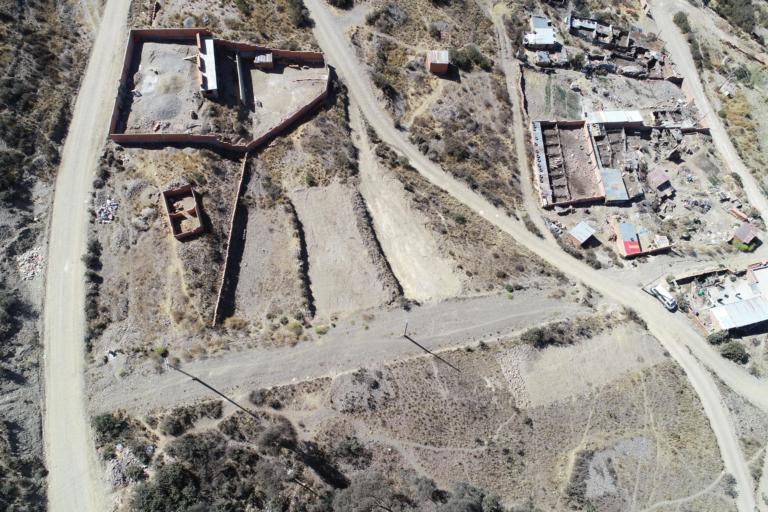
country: BO
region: La Paz
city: La Paz
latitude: -16.5422
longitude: -68.1537
